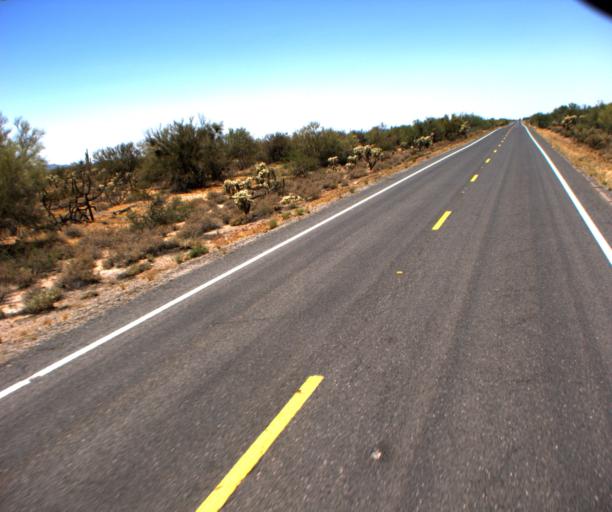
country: US
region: Arizona
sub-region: Pinal County
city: Florence
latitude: 32.8427
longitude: -111.2233
